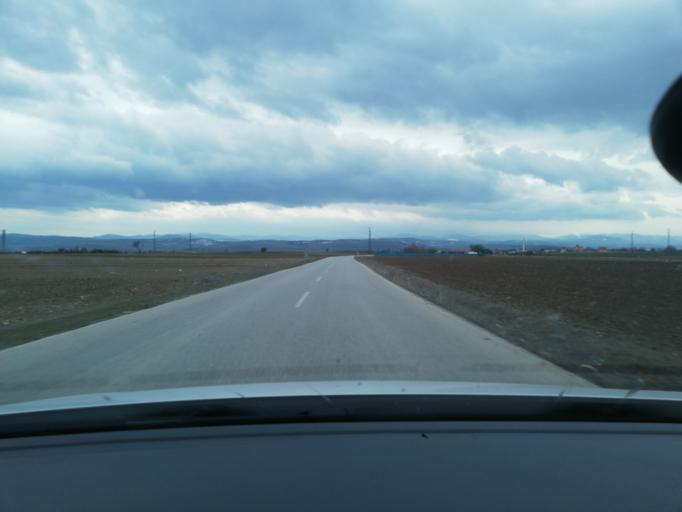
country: TR
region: Bolu
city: Gerede
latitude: 40.7675
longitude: 32.2015
